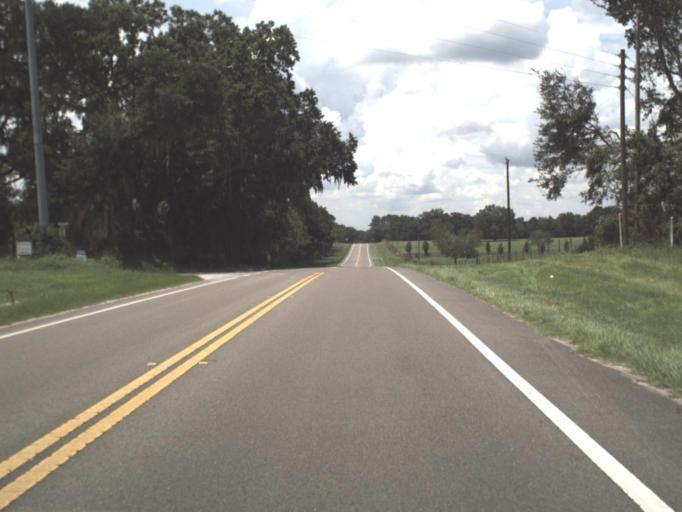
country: US
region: Florida
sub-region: Levy County
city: Williston
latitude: 29.4106
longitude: -82.4529
